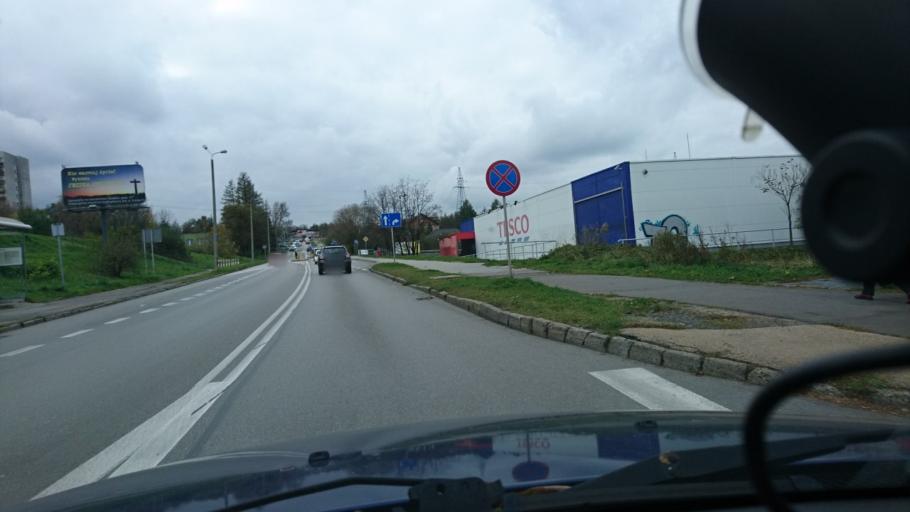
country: PL
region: Silesian Voivodeship
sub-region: Bielsko-Biala
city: Bielsko-Biala
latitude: 49.8097
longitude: 19.0230
